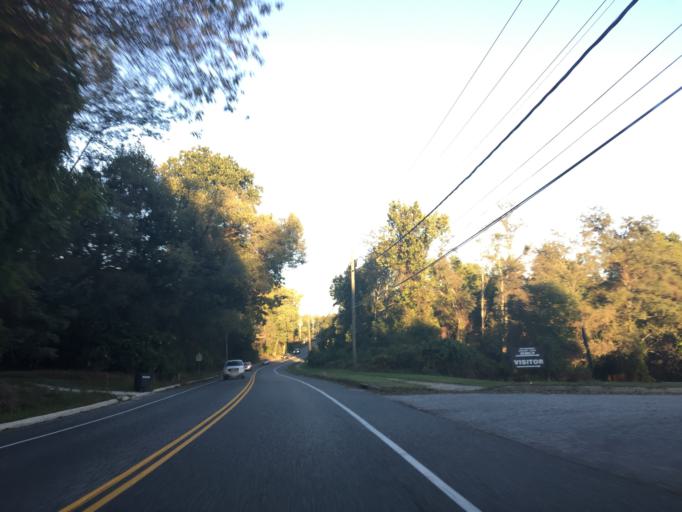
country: US
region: Maryland
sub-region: Harford County
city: Bel Air South
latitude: 39.4785
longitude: -76.3245
